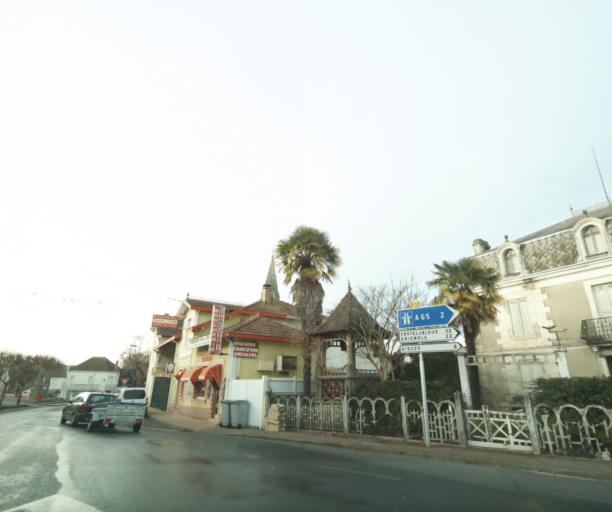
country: FR
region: Aquitaine
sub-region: Departement de la Gironde
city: Prechac
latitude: 44.2917
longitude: -0.2604
